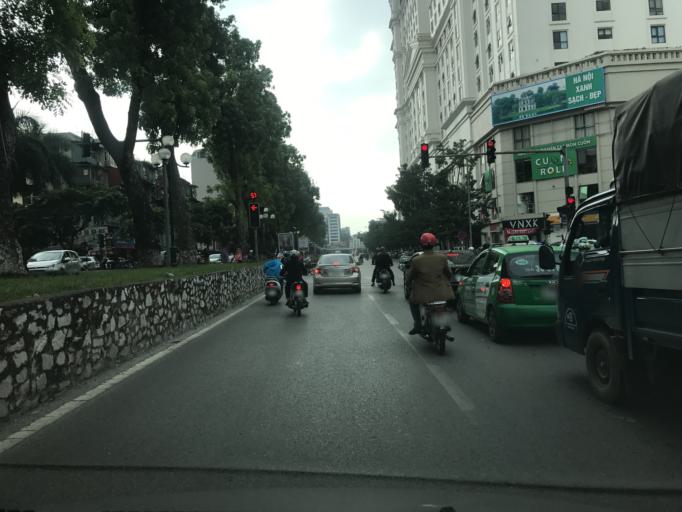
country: VN
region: Ha Noi
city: Dong Da
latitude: 21.0266
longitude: 105.8235
